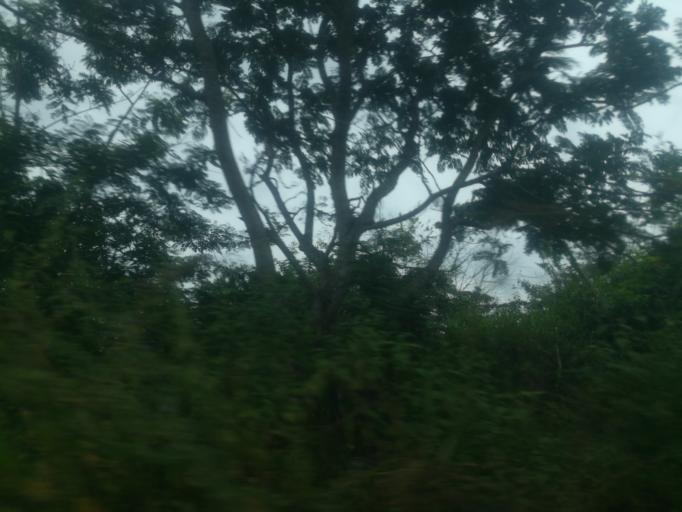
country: NG
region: Ogun
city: Itori
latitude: 7.0999
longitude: 3.1585
